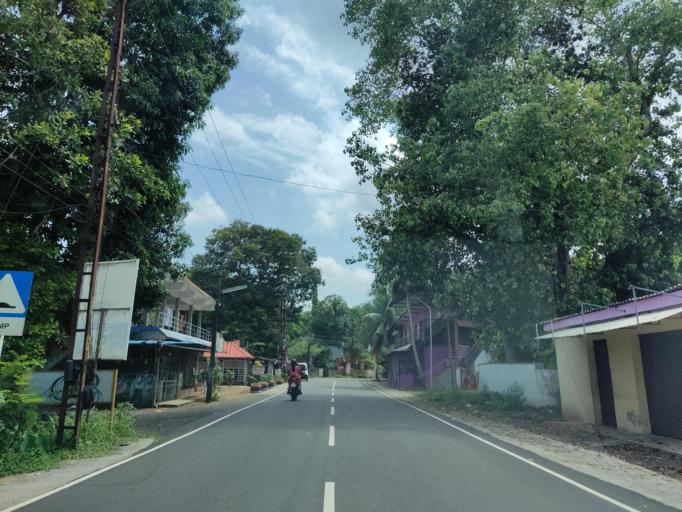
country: IN
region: Kerala
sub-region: Alappuzha
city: Mavelikara
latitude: 9.2679
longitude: 76.5649
